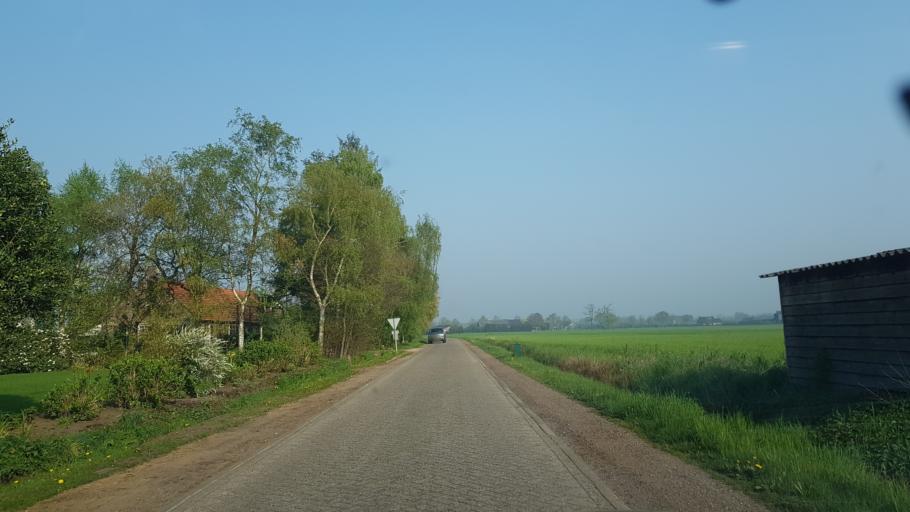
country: NL
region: North Brabant
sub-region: Gemeente Someren
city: Someren
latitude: 51.3717
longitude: 5.7007
